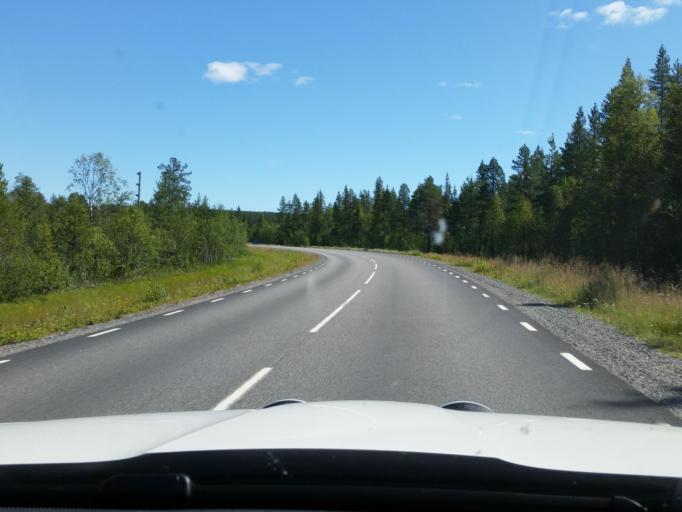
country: SE
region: Vaesterbotten
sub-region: Skelleftea Kommun
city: Storvik
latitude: 65.3252
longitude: 20.6947
